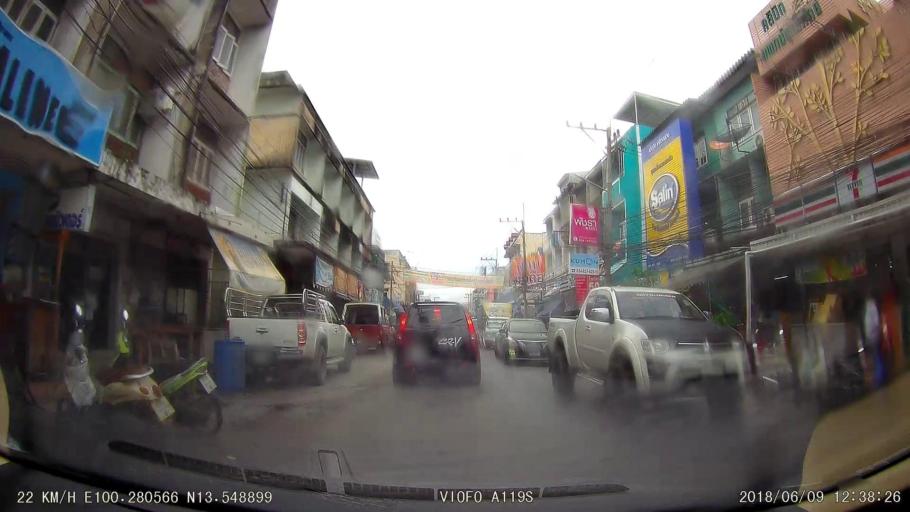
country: TH
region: Samut Sakhon
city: Samut Sakhon
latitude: 13.5486
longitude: 100.2804
